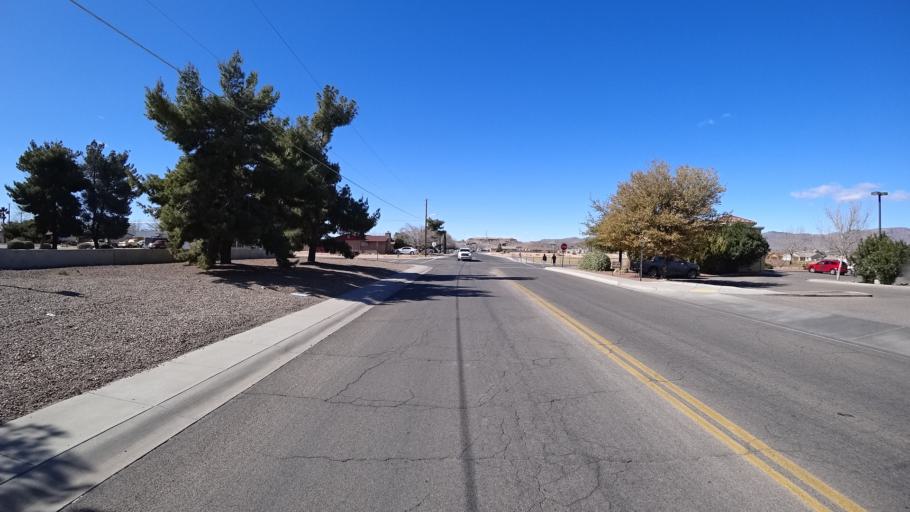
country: US
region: Arizona
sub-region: Mohave County
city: Kingman
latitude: 35.1959
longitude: -114.0110
